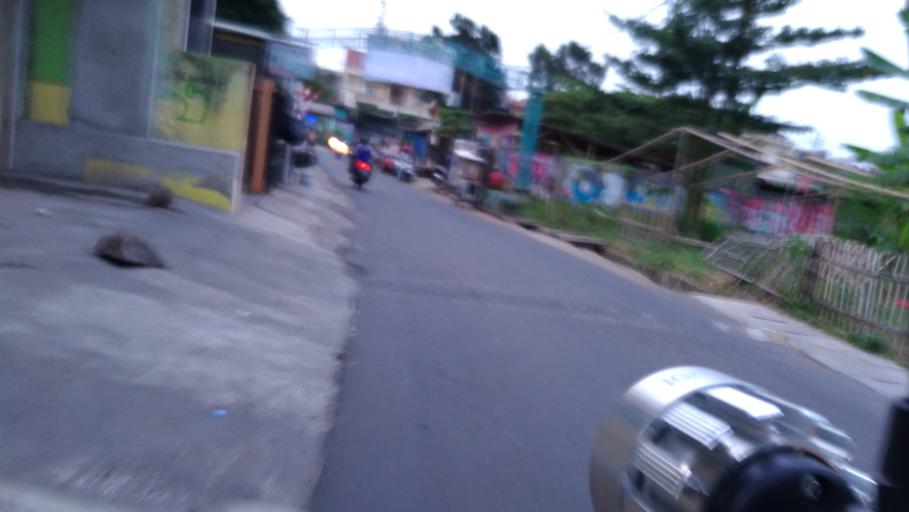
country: ID
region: West Java
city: Depok
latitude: -6.3503
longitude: 106.8727
